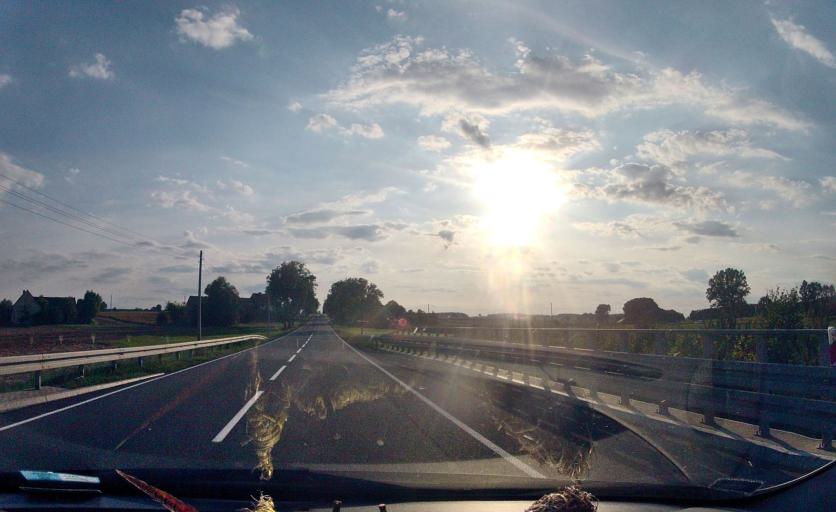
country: PL
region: Opole Voivodeship
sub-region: Powiat oleski
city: Gorzow Slaski
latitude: 51.0129
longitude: 18.3781
